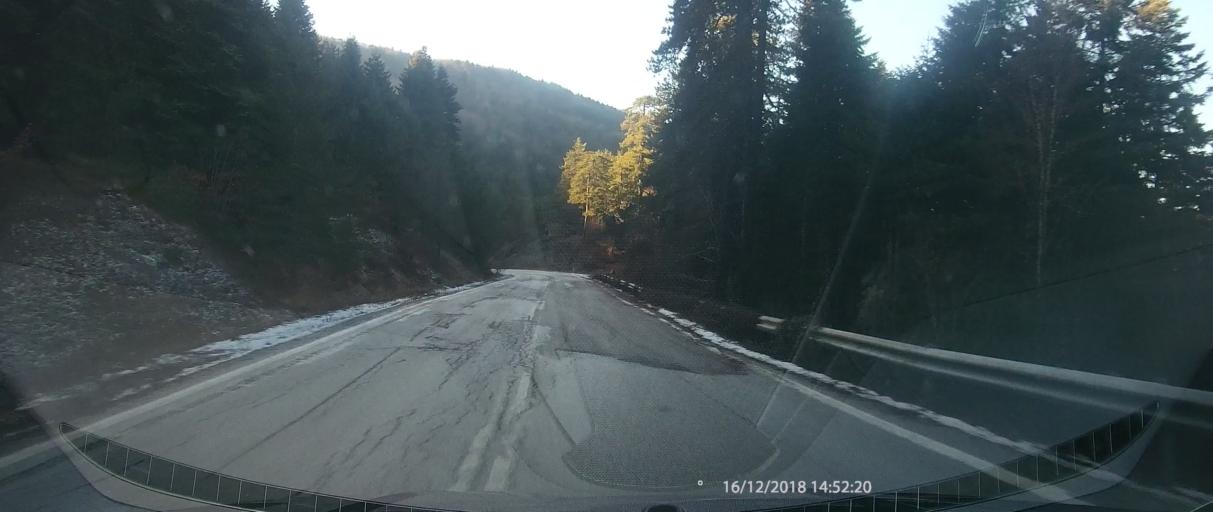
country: GR
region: West Macedonia
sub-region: Nomos Kastorias
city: Nestorio
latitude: 40.2049
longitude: 21.0632
